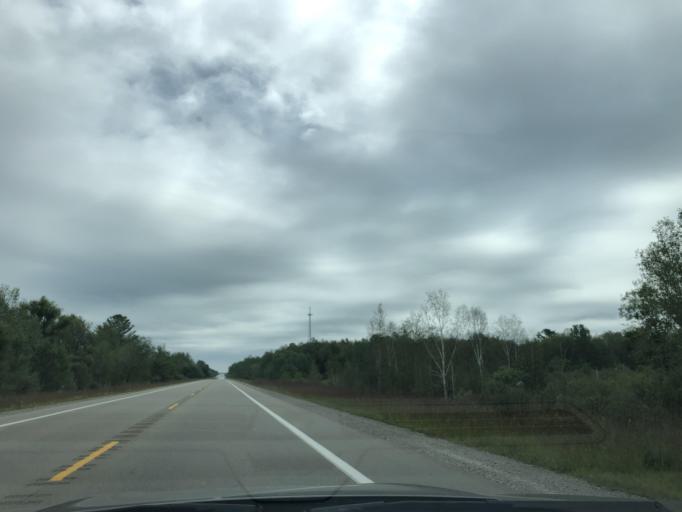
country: US
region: Michigan
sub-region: Clare County
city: Harrison
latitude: 44.0311
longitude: -84.9813
